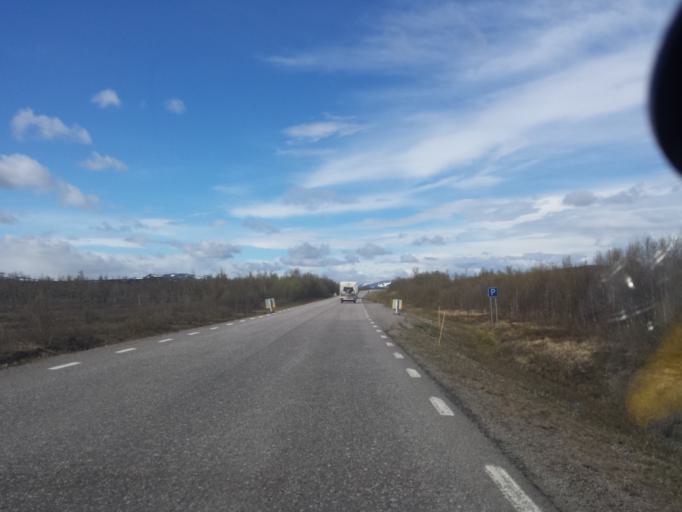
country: SE
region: Norrbotten
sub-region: Kiruna Kommun
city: Kiruna
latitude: 68.0145
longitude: 19.8408
